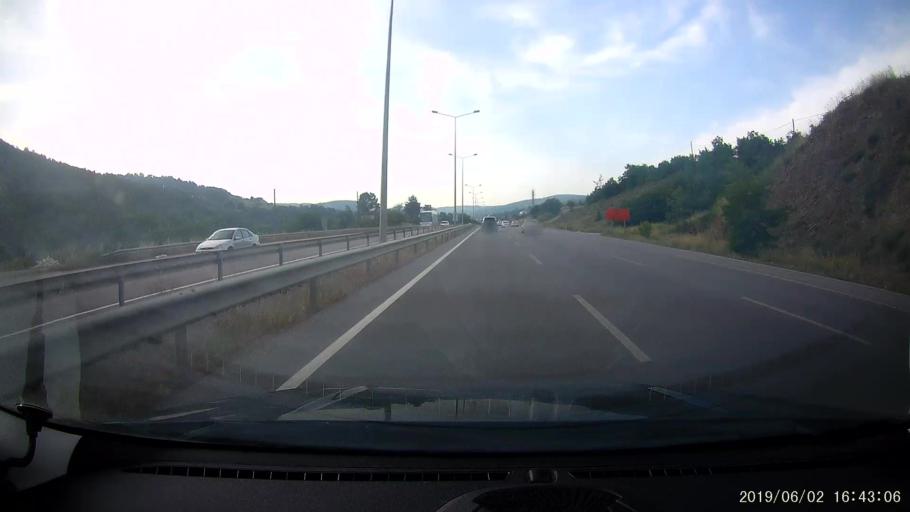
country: TR
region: Samsun
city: Kavak
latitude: 41.1296
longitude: 36.1340
